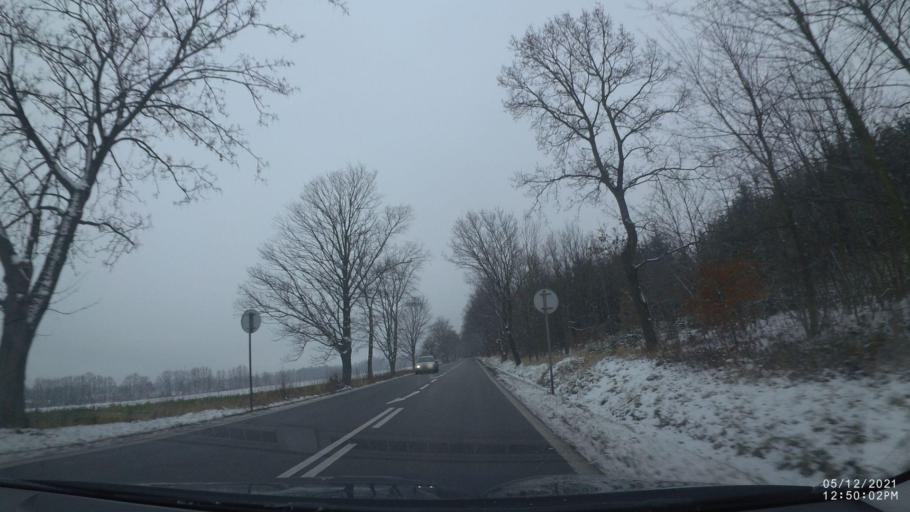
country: CZ
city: Nove Mesto nad Metuji
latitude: 50.3809
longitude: 16.1441
